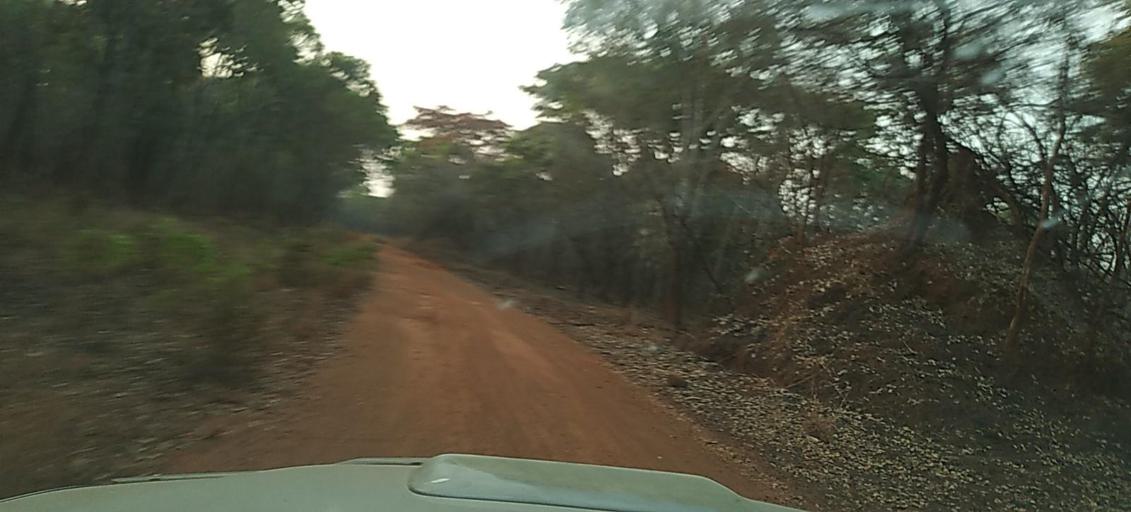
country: ZM
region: North-Western
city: Kasempa
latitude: -13.0882
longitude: 26.3984
